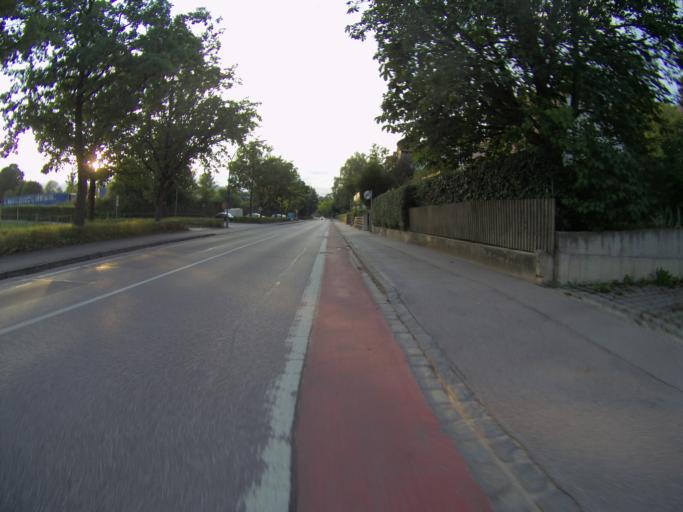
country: DE
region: Bavaria
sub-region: Upper Bavaria
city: Freising
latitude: 48.4057
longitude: 11.7322
